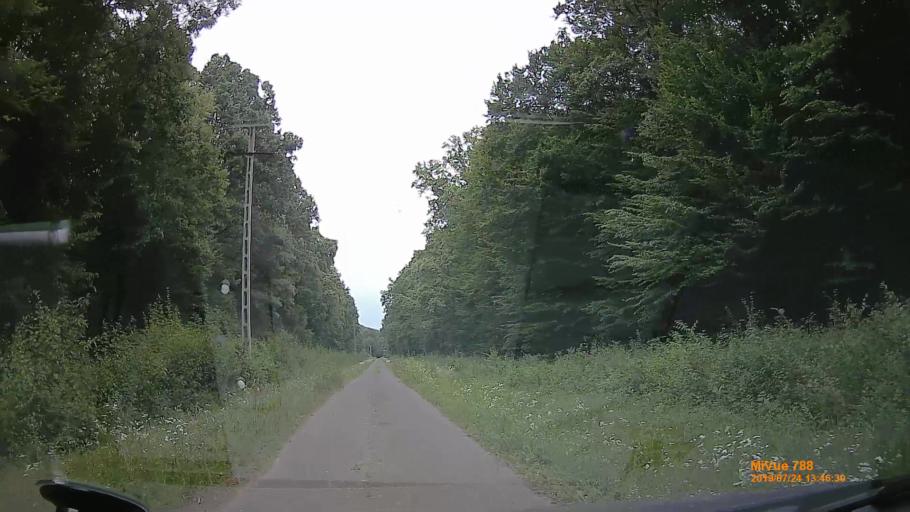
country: HU
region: Szabolcs-Szatmar-Bereg
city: Aranyosapati
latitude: 48.2669
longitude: 22.3420
